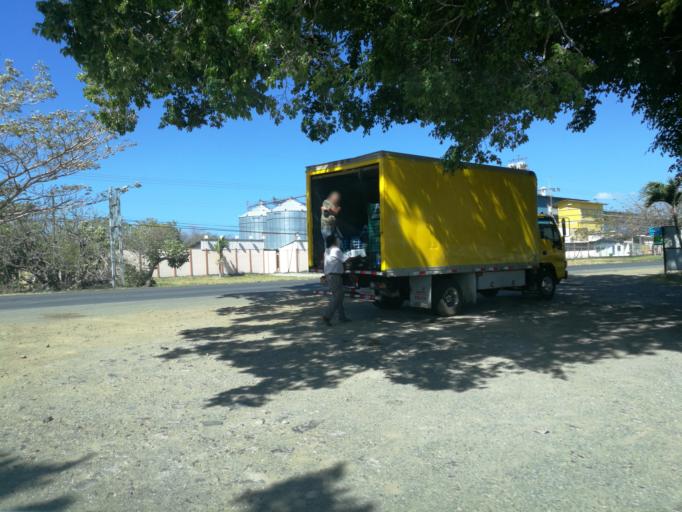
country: CR
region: Guanacaste
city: Liberia
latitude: 10.6608
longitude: -85.4701
